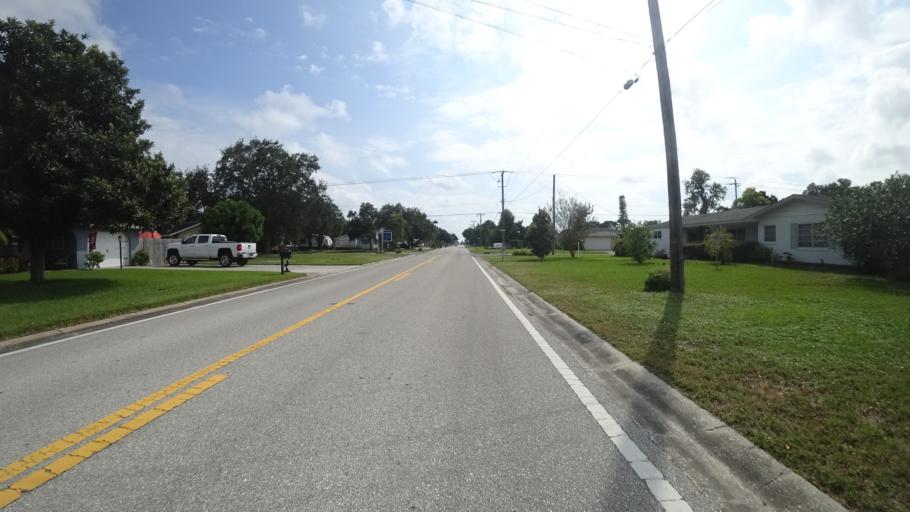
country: US
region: Florida
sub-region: Manatee County
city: West Bradenton
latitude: 27.5043
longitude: -82.6203
